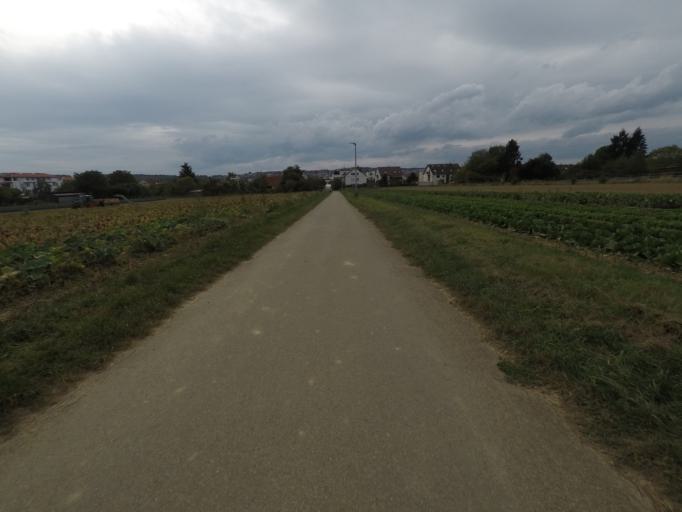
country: DE
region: Baden-Wuerttemberg
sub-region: Regierungsbezirk Stuttgart
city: Filderstadt
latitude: 48.6525
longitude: 9.2258
